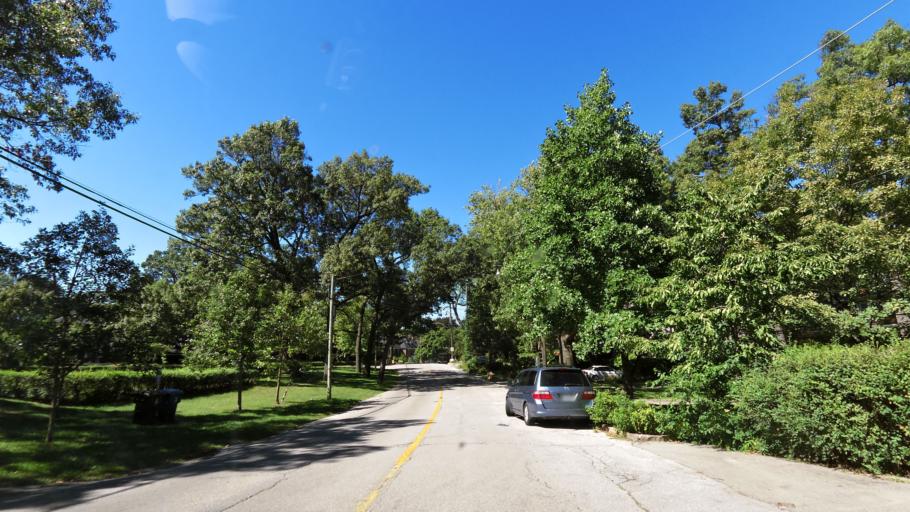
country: CA
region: Ontario
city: Etobicoke
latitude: 43.6424
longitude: -79.4829
